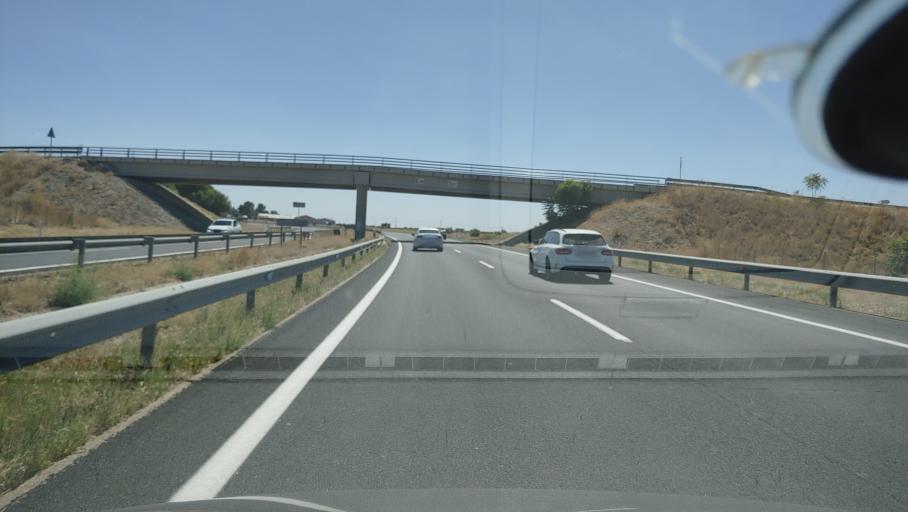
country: ES
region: Castille-La Mancha
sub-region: Provincia de Ciudad Real
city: Villarta de San Juan
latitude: 39.2217
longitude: -3.4136
